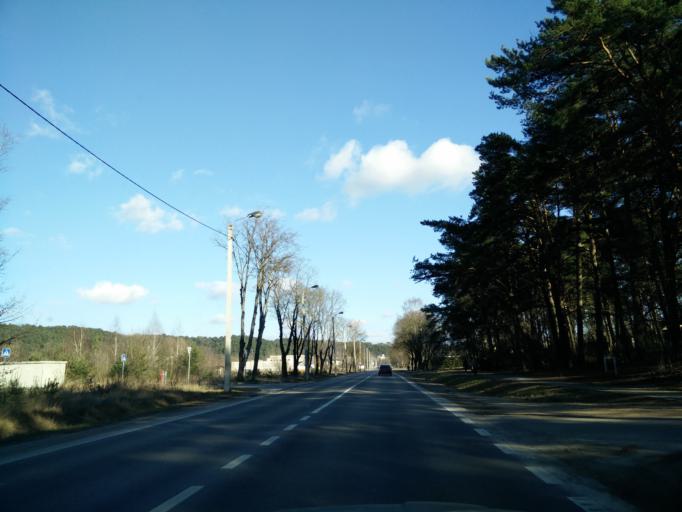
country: LT
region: Kauno apskritis
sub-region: Kauno rajonas
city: Akademija (Kaunas)
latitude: 54.9207
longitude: 23.8125
